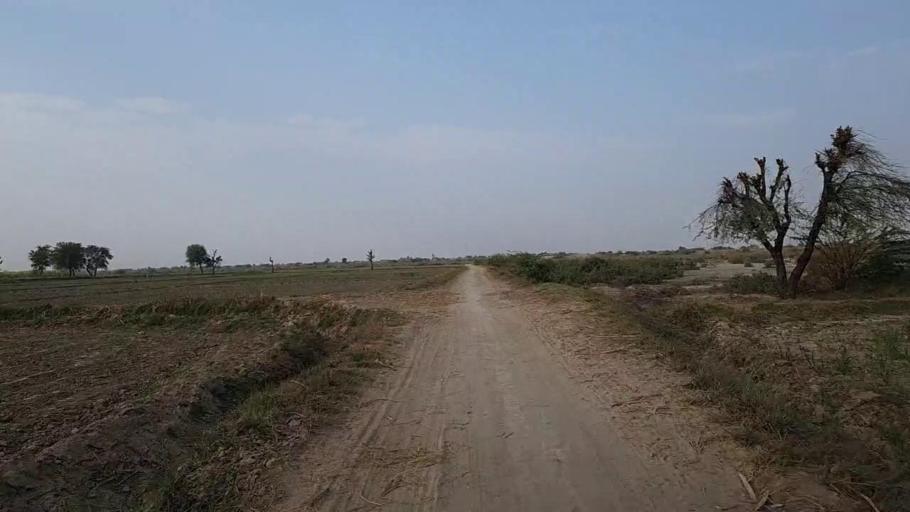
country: PK
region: Sindh
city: Pithoro
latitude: 25.4362
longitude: 69.2371
